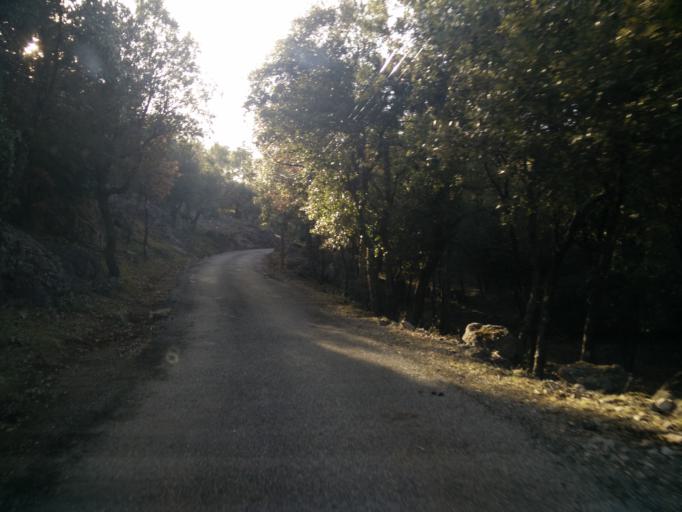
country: FR
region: Provence-Alpes-Cote d'Azur
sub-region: Departement du Var
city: Belgentier
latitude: 43.2180
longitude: 5.9801
